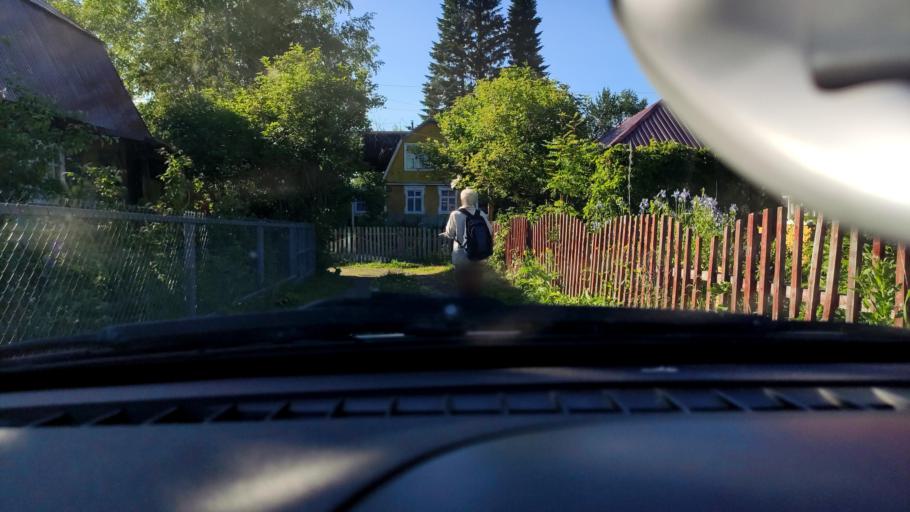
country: RU
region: Perm
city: Bershet'
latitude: 57.7010
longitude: 56.4088
